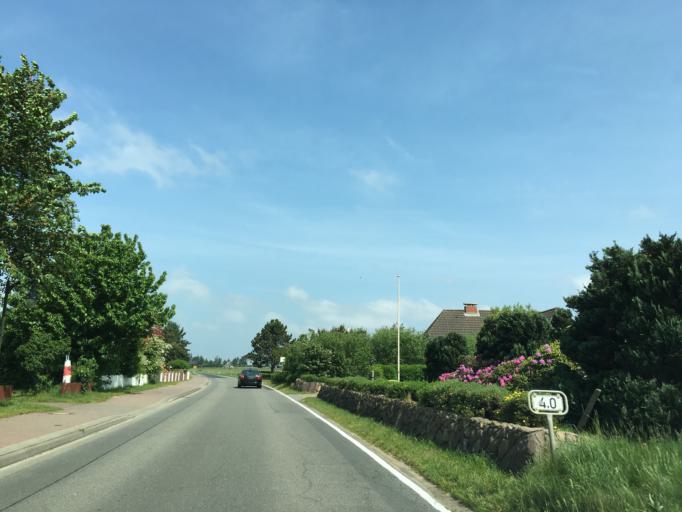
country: DE
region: Schleswig-Holstein
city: Nebel
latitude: 54.6422
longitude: 8.3555
